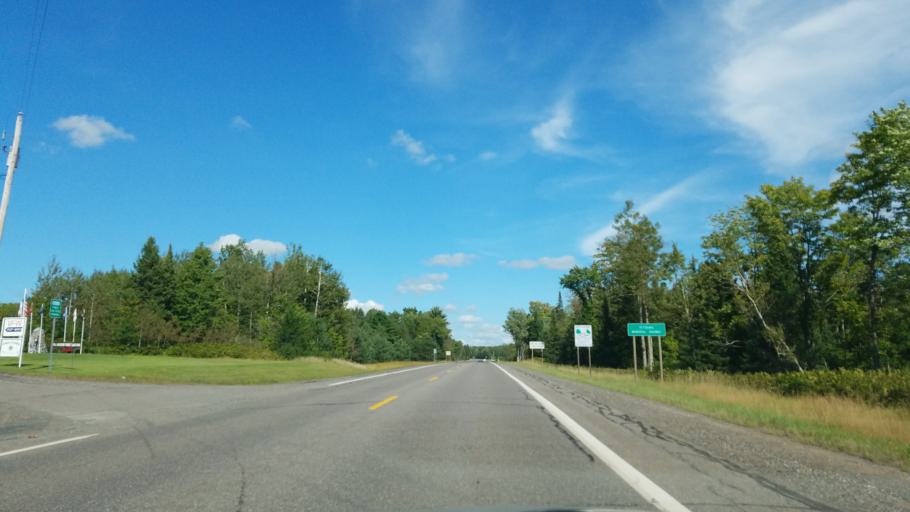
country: US
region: Michigan
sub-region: Baraga County
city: L'Anse
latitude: 46.5474
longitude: -88.5338
